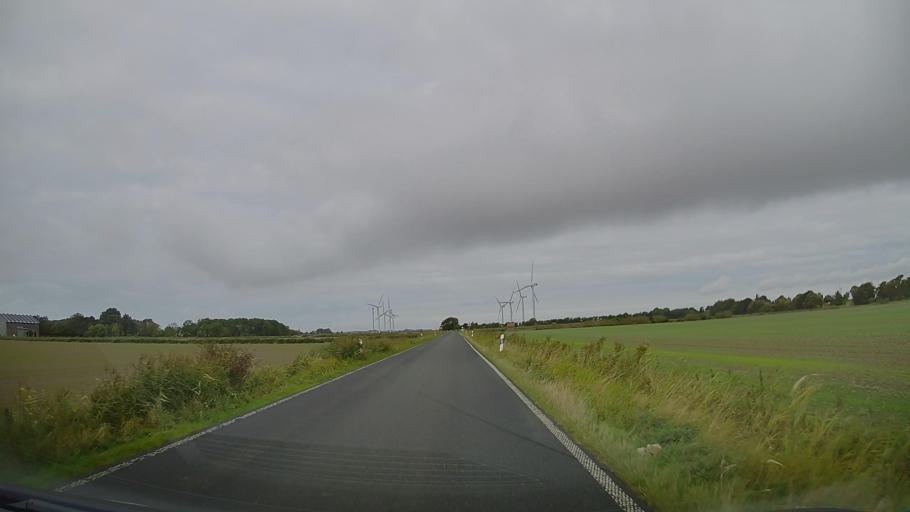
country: DE
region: Schleswig-Holstein
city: Galmsbull
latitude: 54.7661
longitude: 8.7181
